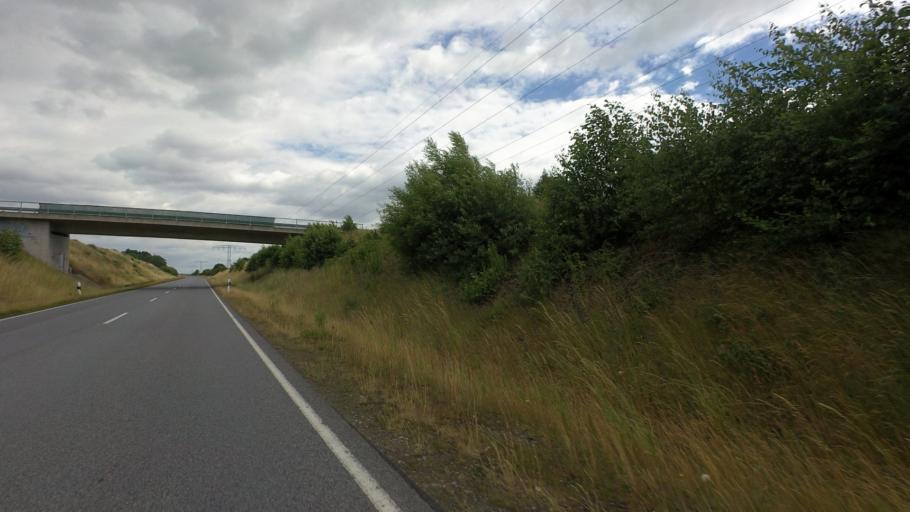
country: DE
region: Saxony
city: Nebelschutz
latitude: 51.2595
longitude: 14.1527
